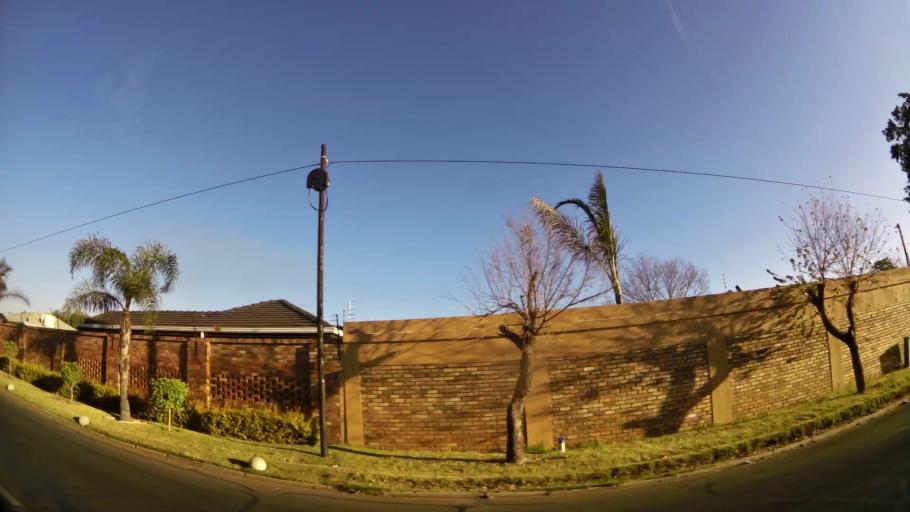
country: ZA
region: Gauteng
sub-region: City of Johannesburg Metropolitan Municipality
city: Roodepoort
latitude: -26.1837
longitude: 27.9171
